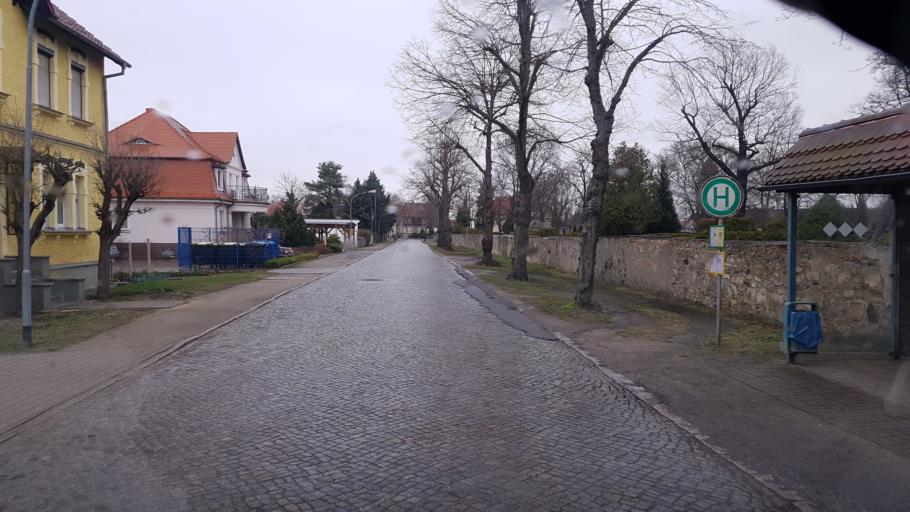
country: DE
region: Brandenburg
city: Ruhland
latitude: 51.4526
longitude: 13.8635
